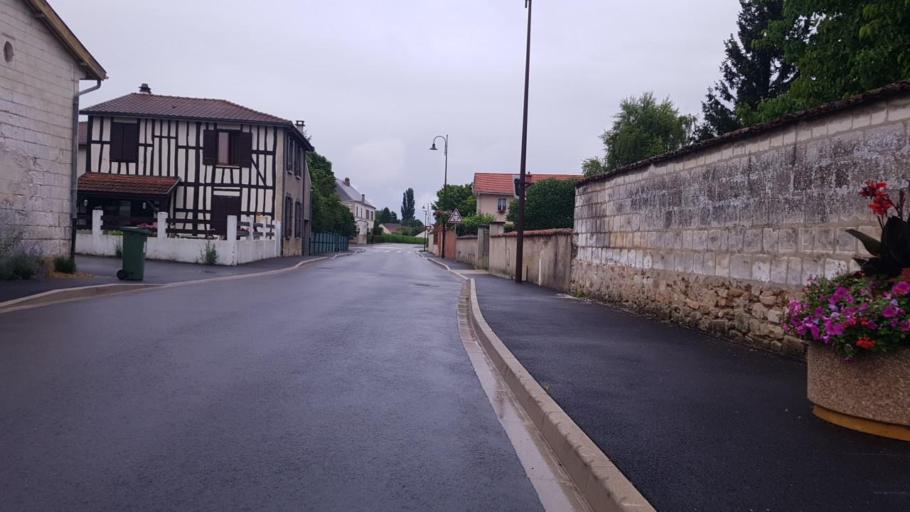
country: FR
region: Champagne-Ardenne
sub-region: Departement de la Marne
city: Sarry
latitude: 48.9205
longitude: 4.4026
